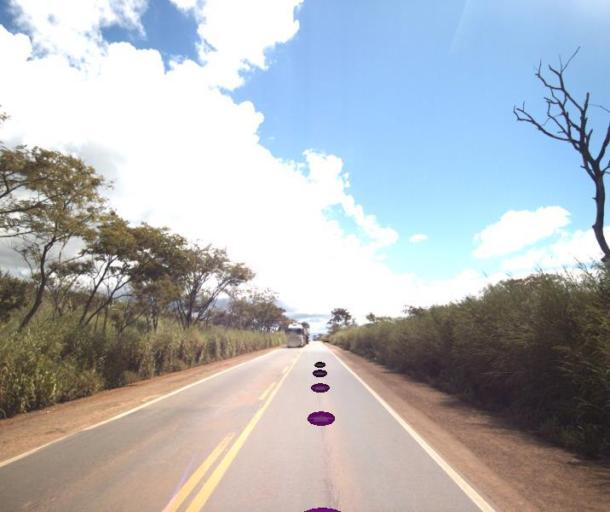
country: BR
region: Goias
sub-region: Anapolis
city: Anapolis
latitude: -16.1617
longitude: -49.0435
